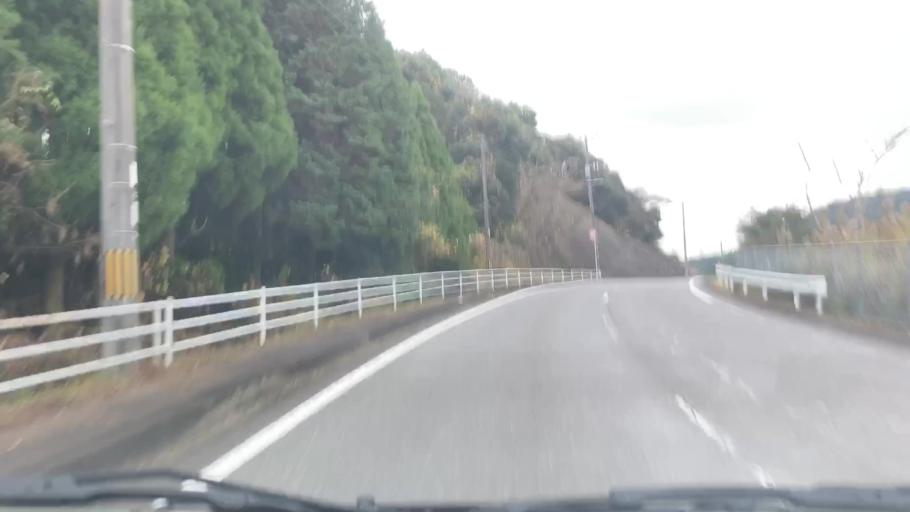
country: JP
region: Saga Prefecture
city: Ureshinomachi-shimojuku
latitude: 33.1115
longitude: 129.9768
